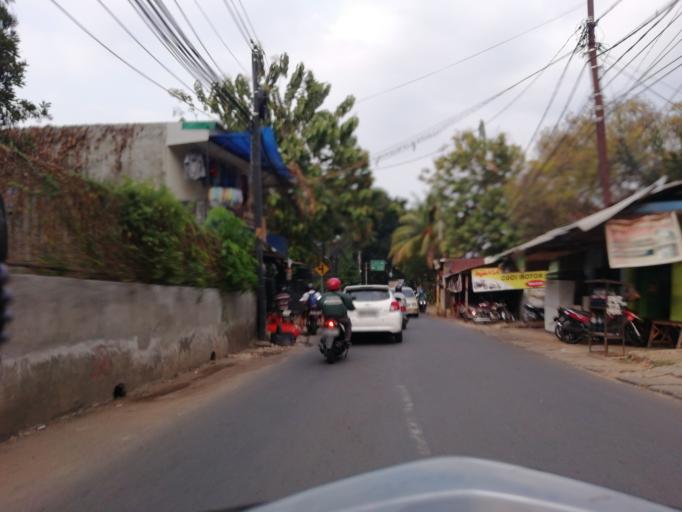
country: ID
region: West Java
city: Depok
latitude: -6.3271
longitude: 106.8151
